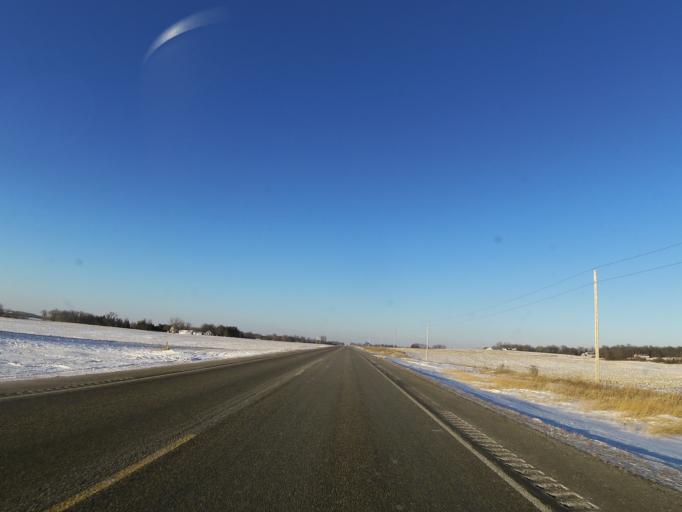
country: US
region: Minnesota
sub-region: Rice County
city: Lonsdale
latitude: 44.4927
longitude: -93.4428
